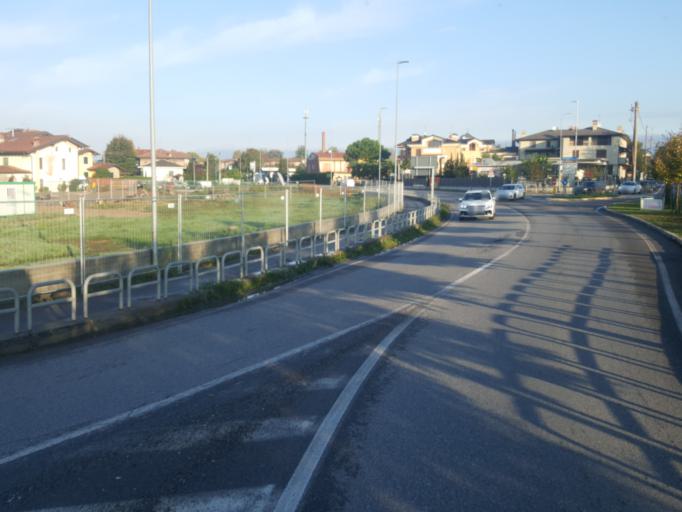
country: IT
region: Lombardy
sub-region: Provincia di Bergamo
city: Cologno al Serio
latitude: 45.5731
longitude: 9.7090
